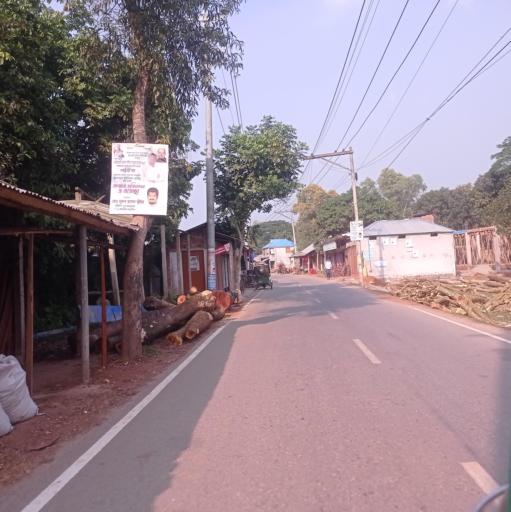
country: BD
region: Dhaka
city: Bhairab Bazar
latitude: 24.0621
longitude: 90.8409
